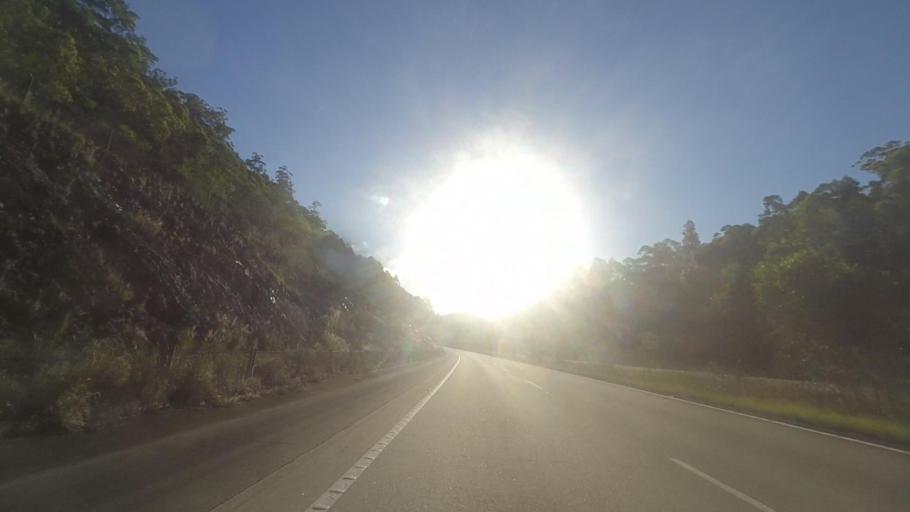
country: AU
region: New South Wales
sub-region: Great Lakes
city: Bulahdelah
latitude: -32.3749
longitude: 152.2792
